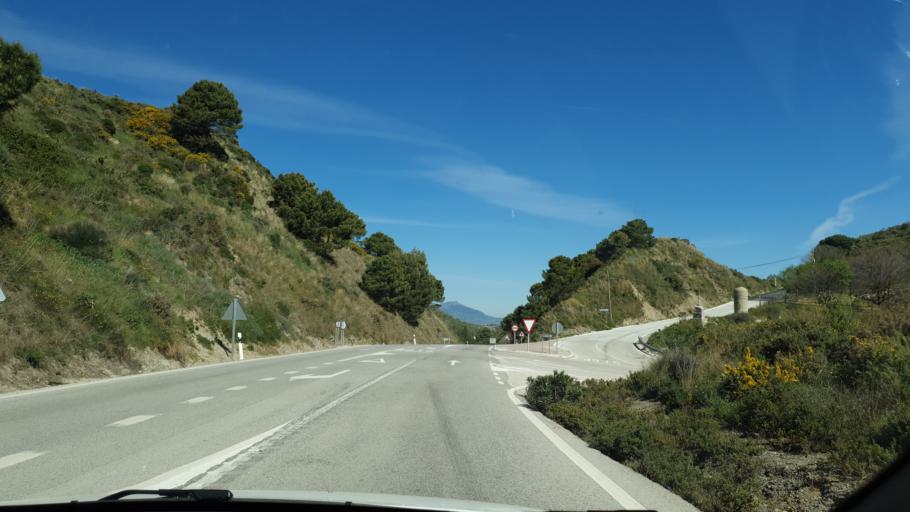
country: ES
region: Andalusia
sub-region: Provincia de Malaga
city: Ojen
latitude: 36.5824
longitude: -4.8528
